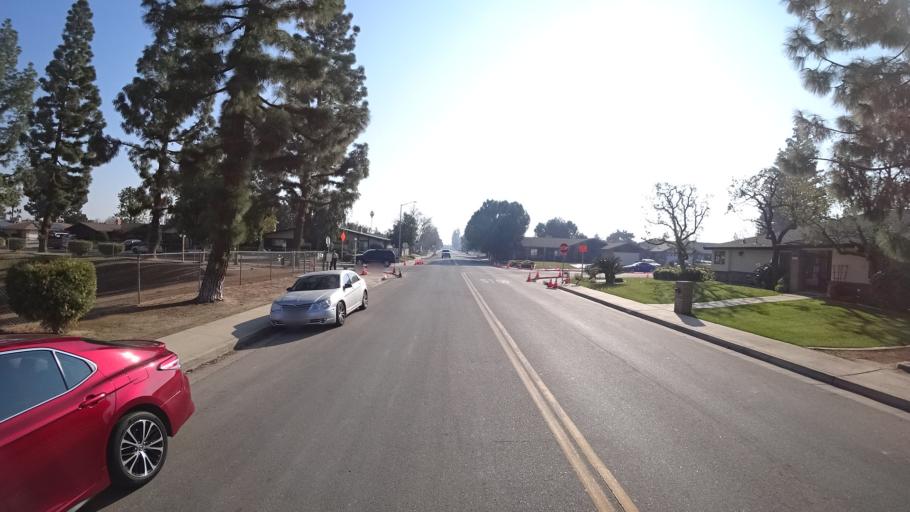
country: US
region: California
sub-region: Kern County
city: Bakersfield
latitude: 35.3592
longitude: -119.0546
